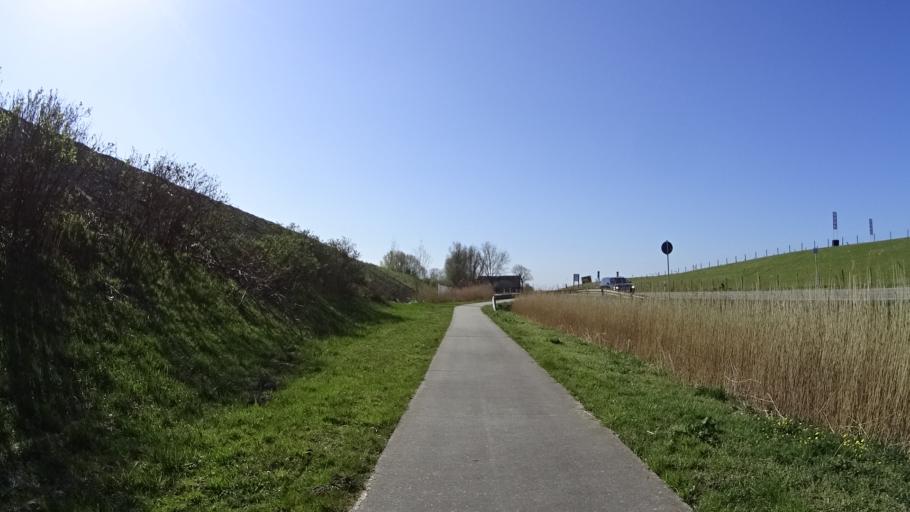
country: DE
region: Lower Saxony
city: Jemgum
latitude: 53.2655
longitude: 7.4075
